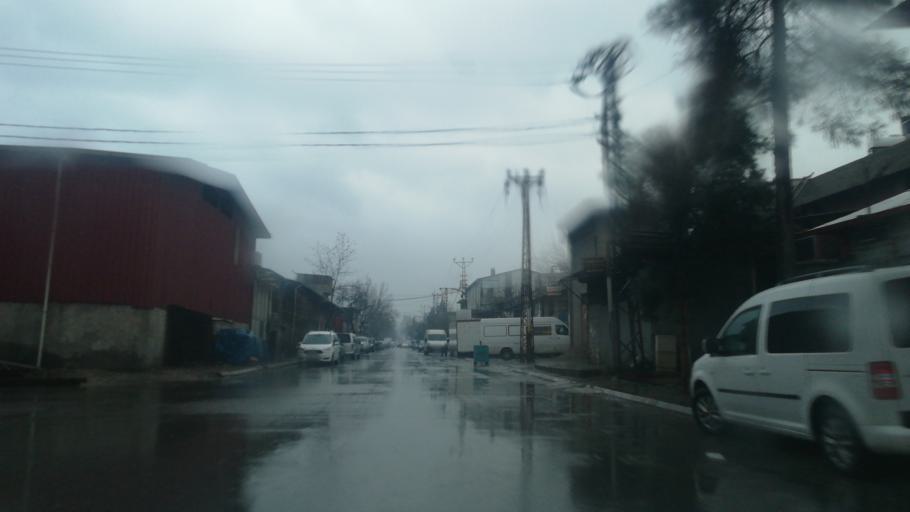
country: TR
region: Kahramanmaras
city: Kahramanmaras
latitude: 37.5596
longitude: 36.9613
